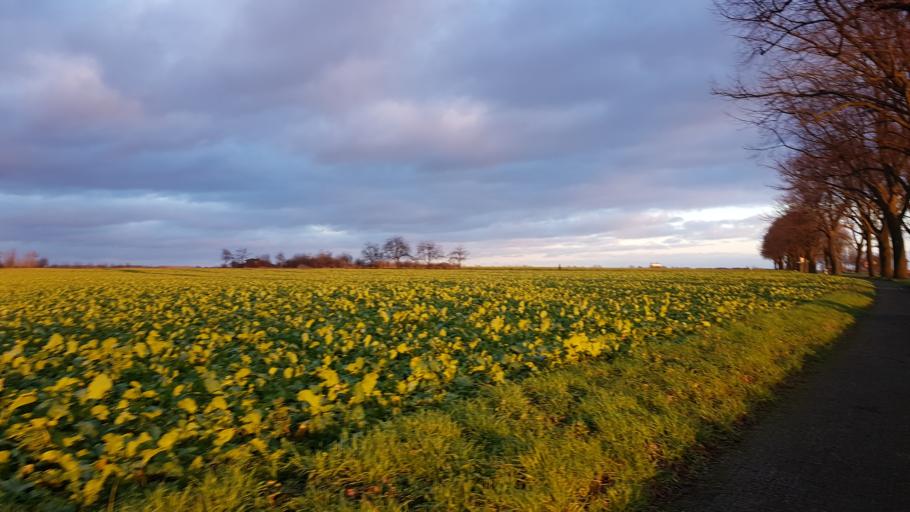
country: DE
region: North Rhine-Westphalia
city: Oer-Erkenschwick
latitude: 51.6626
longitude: 7.3167
